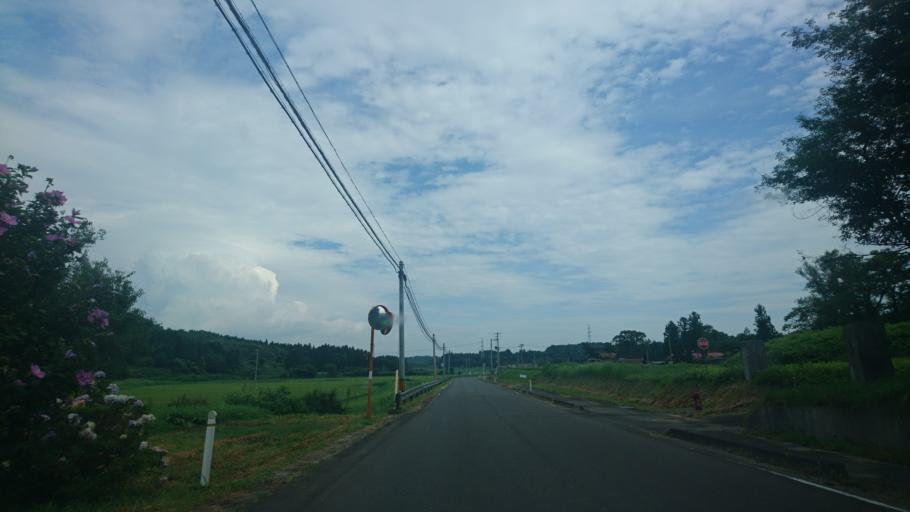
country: JP
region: Miyagi
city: Furukawa
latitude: 38.7667
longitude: 140.9645
